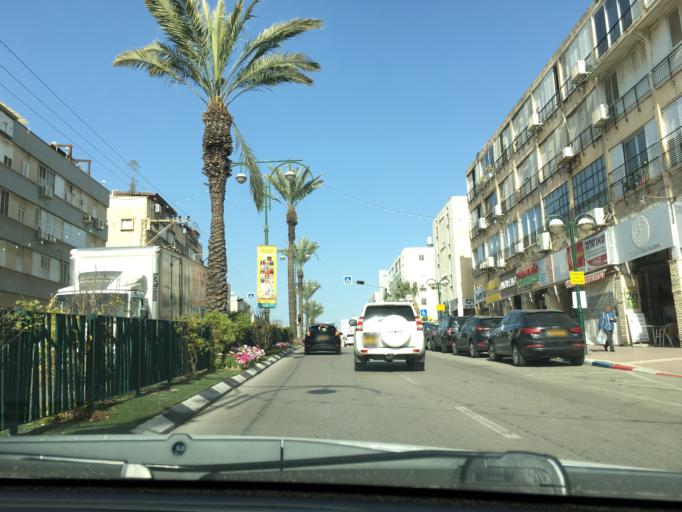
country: IL
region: Tel Aviv
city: Ramat HaSharon
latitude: 32.1438
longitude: 34.8377
